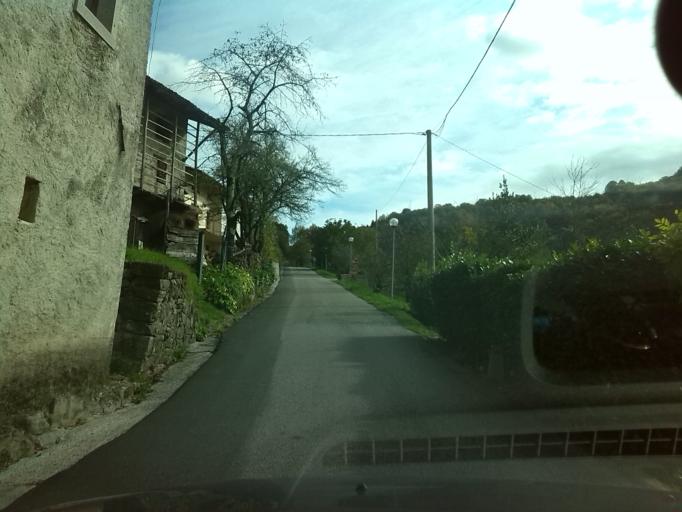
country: IT
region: Friuli Venezia Giulia
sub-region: Provincia di Udine
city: Stregna
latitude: 46.1267
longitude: 13.5785
